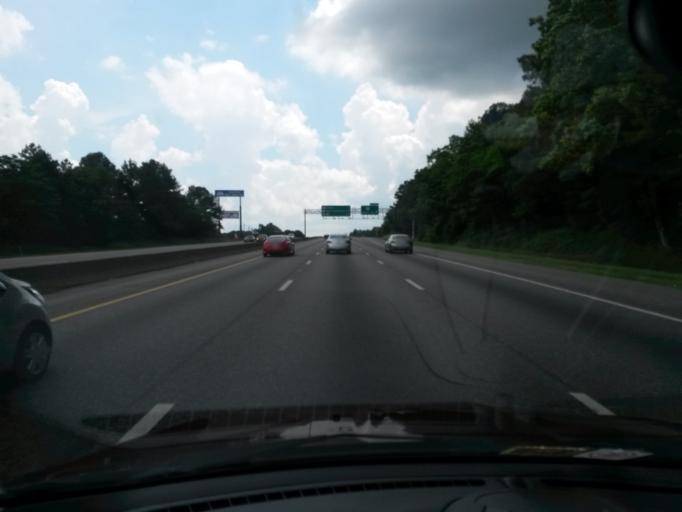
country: US
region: Virginia
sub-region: Chesterfield County
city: Bellwood
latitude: 37.4055
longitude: -77.4256
